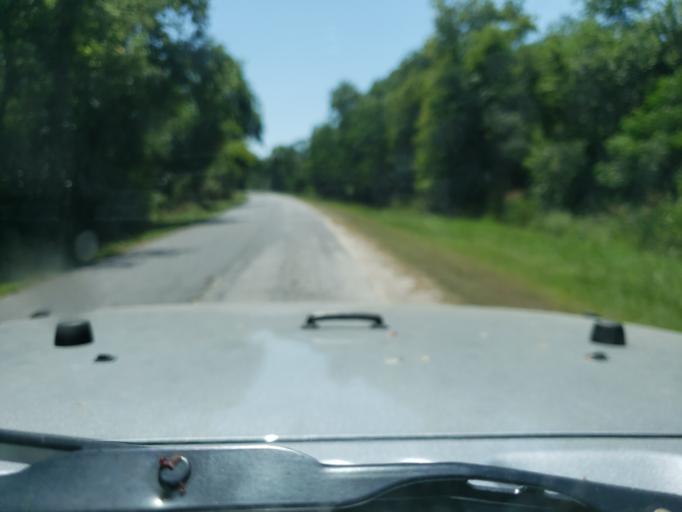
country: US
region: Georgia
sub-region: Chatham County
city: Thunderbolt
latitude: 32.0806
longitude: -81.0380
